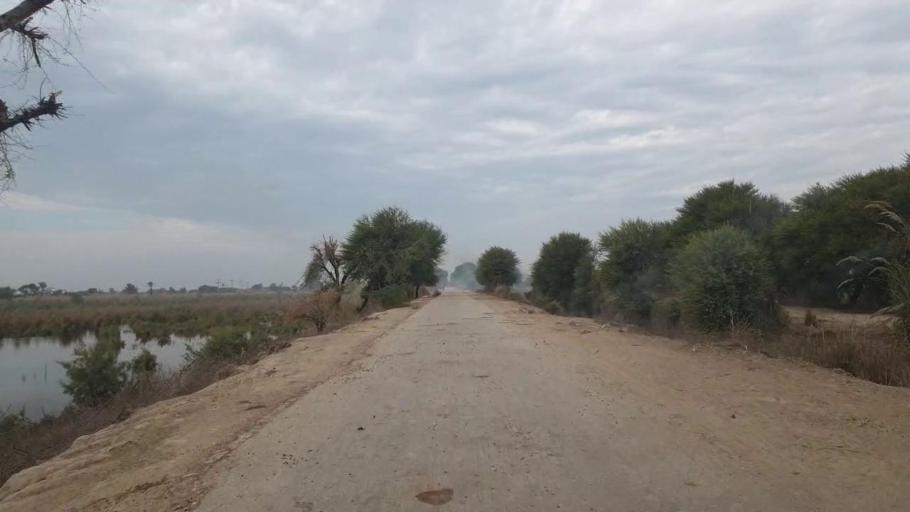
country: PK
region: Sindh
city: Jhol
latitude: 25.9923
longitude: 68.8938
